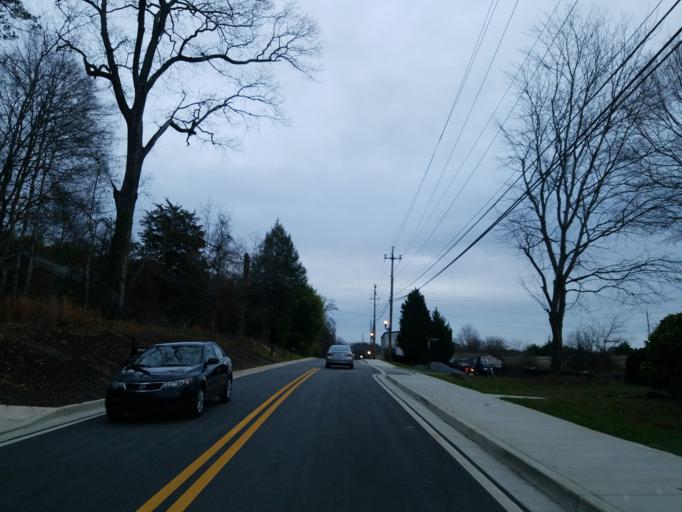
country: US
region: Georgia
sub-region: Cobb County
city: Acworth
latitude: 34.0650
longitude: -84.6724
